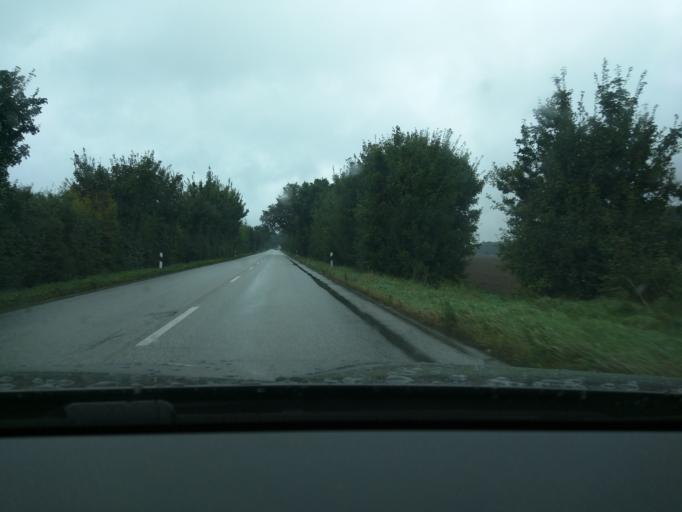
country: DE
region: Schleswig-Holstein
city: Kruzen
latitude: 53.4090
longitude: 10.5375
